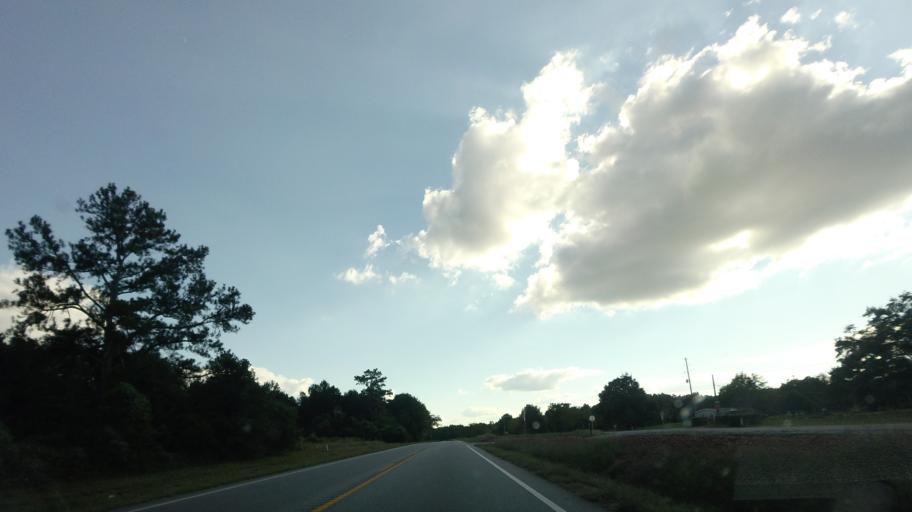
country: US
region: Georgia
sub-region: Lamar County
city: Barnesville
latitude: 33.0205
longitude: -84.1833
